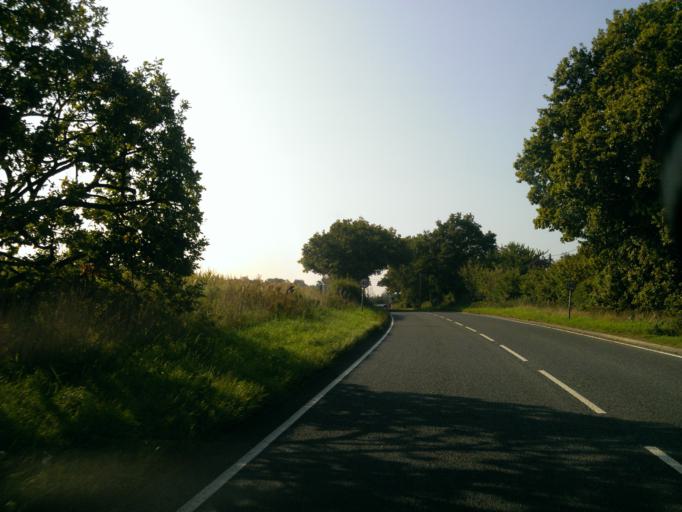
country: GB
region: England
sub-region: Essex
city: Eight Ash Green
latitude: 51.8580
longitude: 0.8202
